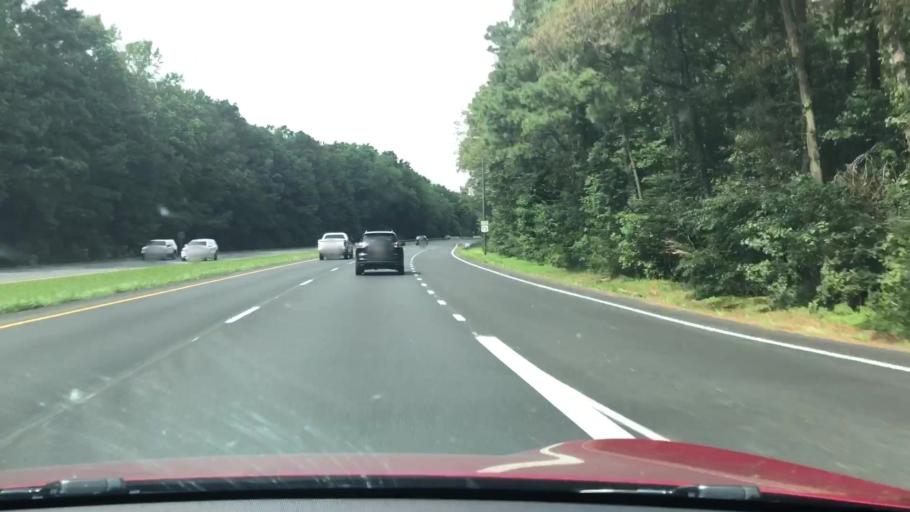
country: US
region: Maryland
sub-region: Worcester County
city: Pocomoke City
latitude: 38.0062
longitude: -75.5445
